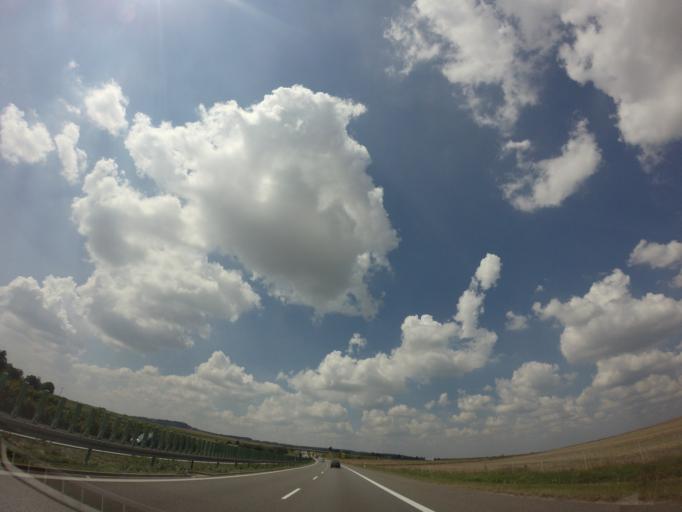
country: PL
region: Opole Voivodeship
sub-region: Powiat strzelecki
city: Lesnica
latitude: 50.4660
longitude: 18.2126
